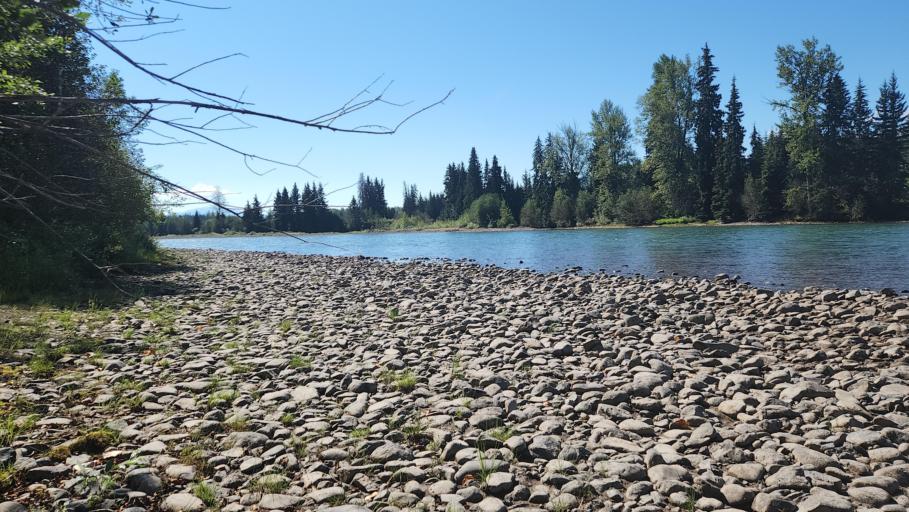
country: CA
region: British Columbia
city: Houston
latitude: 54.5160
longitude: -126.8390
